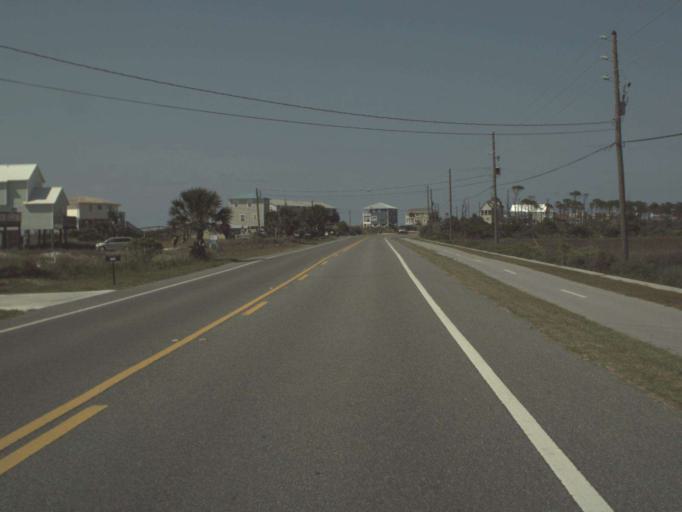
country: US
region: Florida
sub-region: Gulf County
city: Port Saint Joe
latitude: 29.6857
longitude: -85.3688
